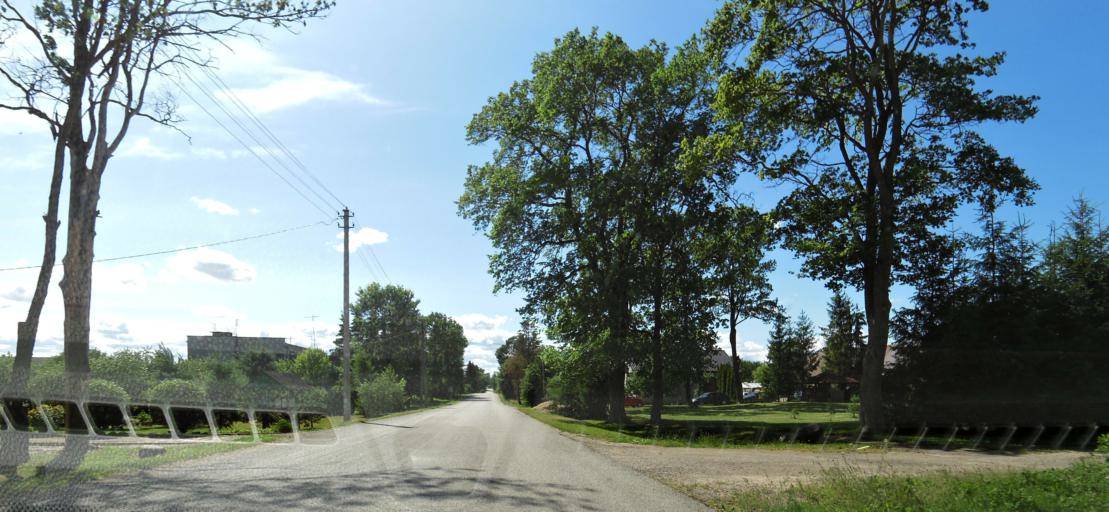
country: LV
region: Bauskas Rajons
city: Bauska
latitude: 56.2516
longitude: 24.2987
